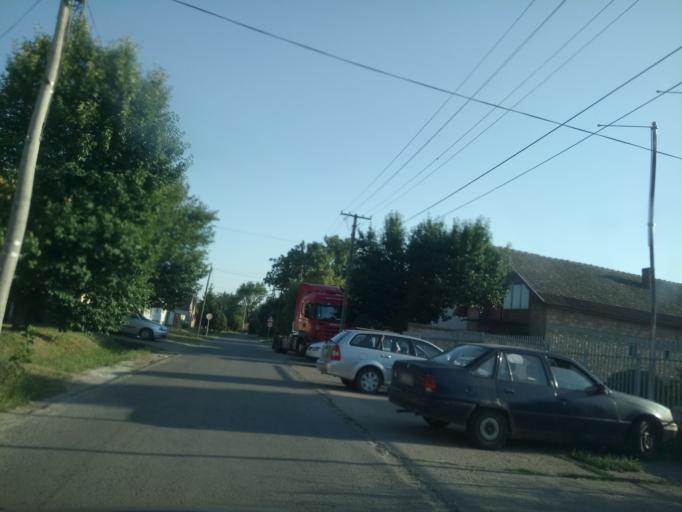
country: RS
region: Autonomna Pokrajina Vojvodina
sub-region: Sremski Okrug
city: Stara Pazova
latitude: 44.9930
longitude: 20.1655
